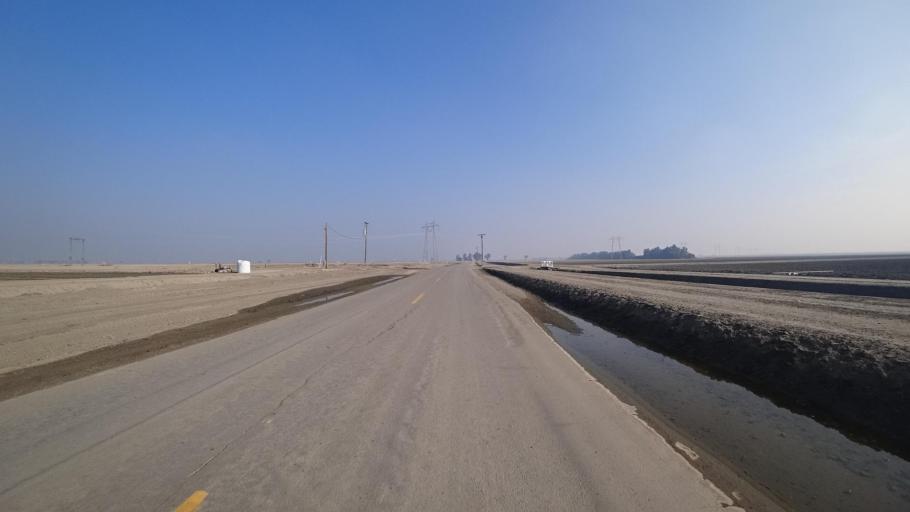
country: US
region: California
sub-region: Kern County
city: Greenfield
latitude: 35.1513
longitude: -119.0228
